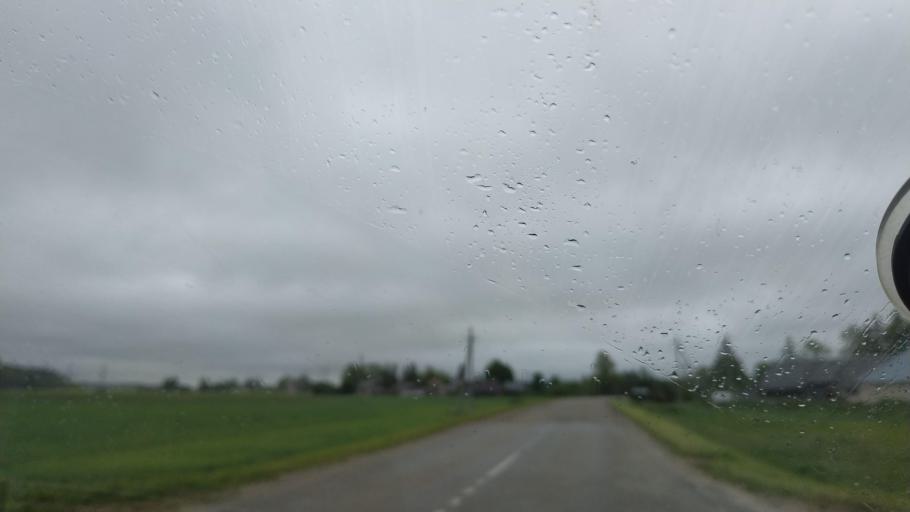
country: LT
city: Vabalninkas
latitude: 56.0011
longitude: 24.6255
